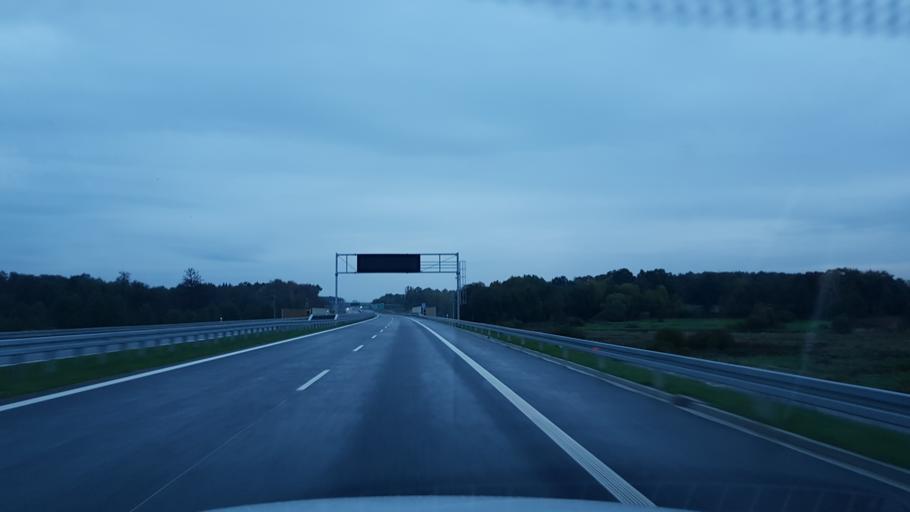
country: PL
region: West Pomeranian Voivodeship
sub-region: Powiat gryficki
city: Brojce
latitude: 53.9291
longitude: 15.3903
